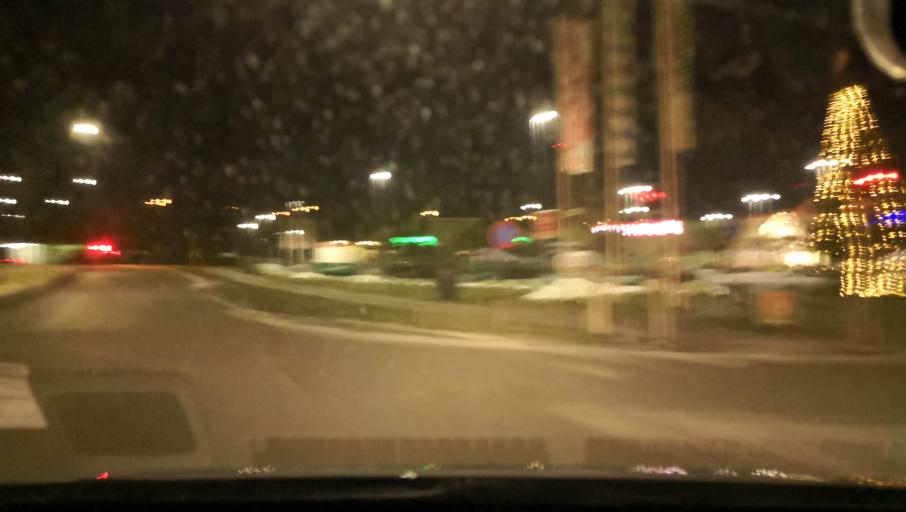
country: SE
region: Stockholm
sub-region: Jarfalla Kommun
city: Jakobsberg
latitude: 59.4225
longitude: 17.8556
